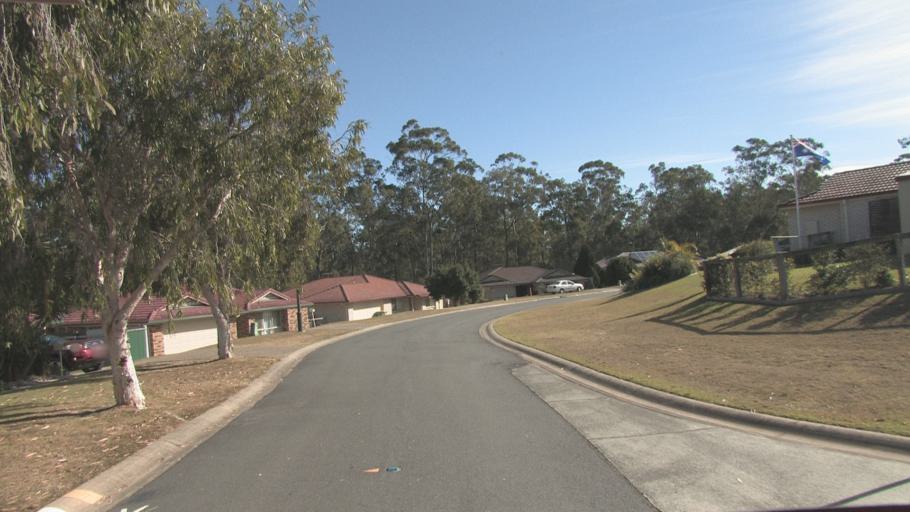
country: AU
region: Queensland
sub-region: Logan
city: North Maclean
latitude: -27.8115
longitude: 152.9513
